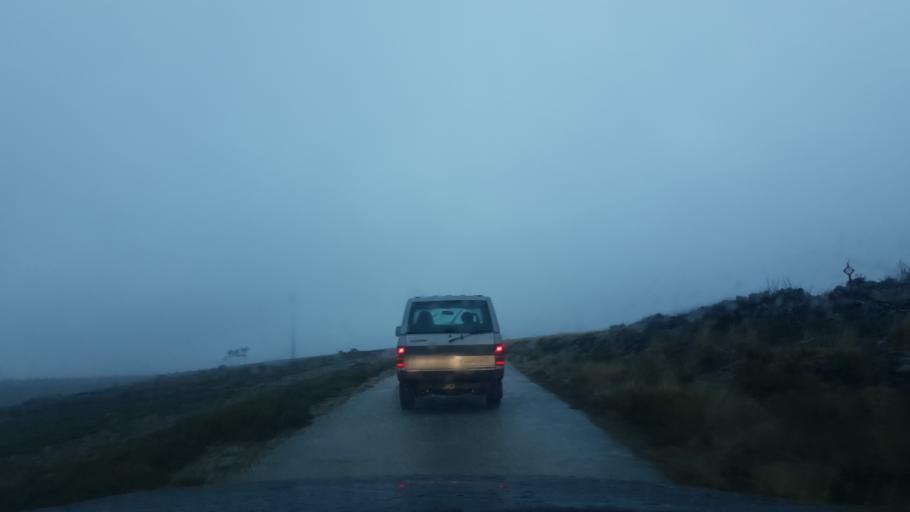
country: PT
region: Viseu
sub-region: Sao Pedro do Sul
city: Sao Pedro do Sul
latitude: 40.8298
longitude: -8.1264
